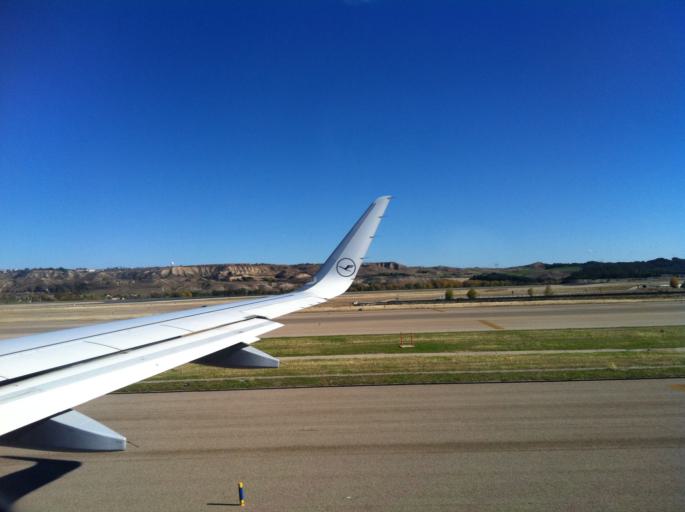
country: ES
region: Madrid
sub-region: Provincia de Madrid
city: Barajas de Madrid
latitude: 40.4906
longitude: -3.5625
